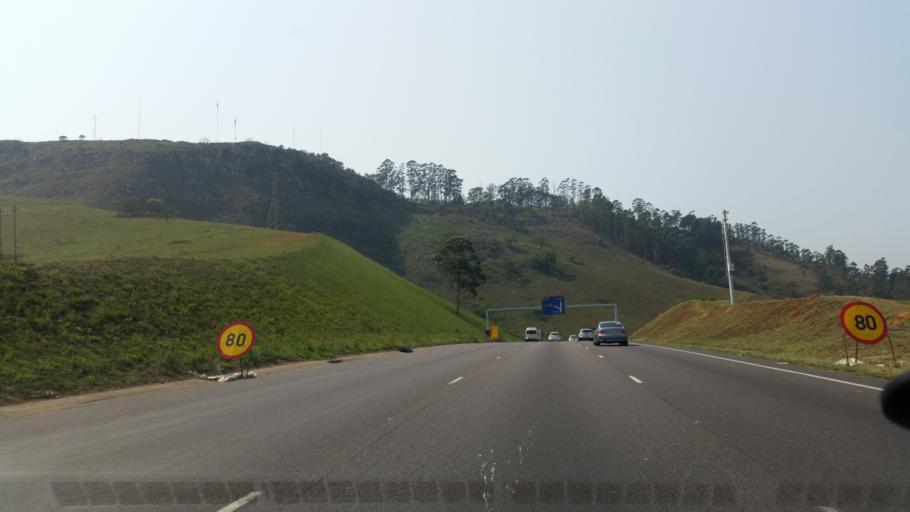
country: ZA
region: KwaZulu-Natal
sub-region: eThekwini Metropolitan Municipality
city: Mpumalanga
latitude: -29.7776
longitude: 30.7076
